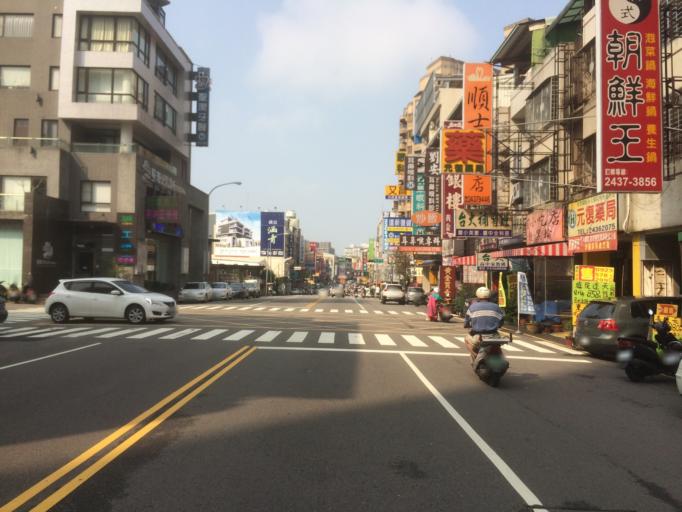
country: TW
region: Taiwan
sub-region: Taichung City
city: Taichung
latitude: 24.1748
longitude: 120.7158
